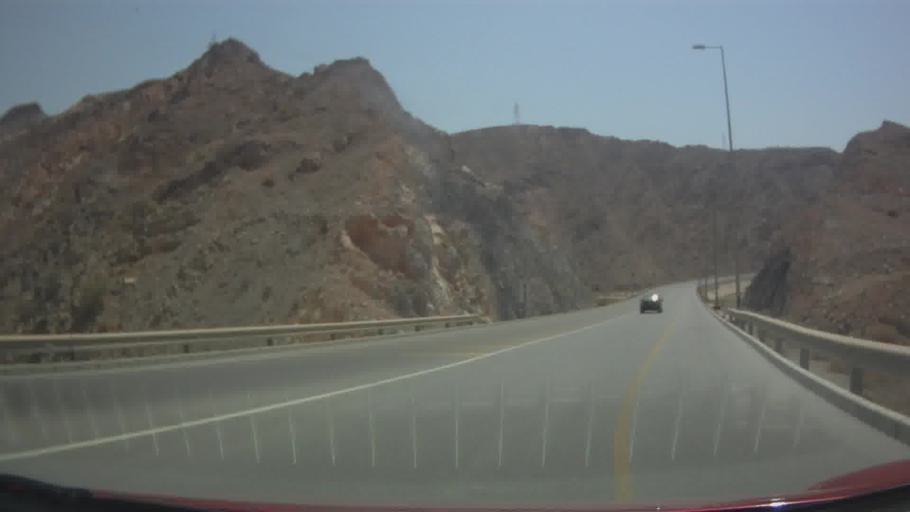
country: OM
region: Muhafazat Masqat
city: Muscat
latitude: 23.5341
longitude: 58.6494
